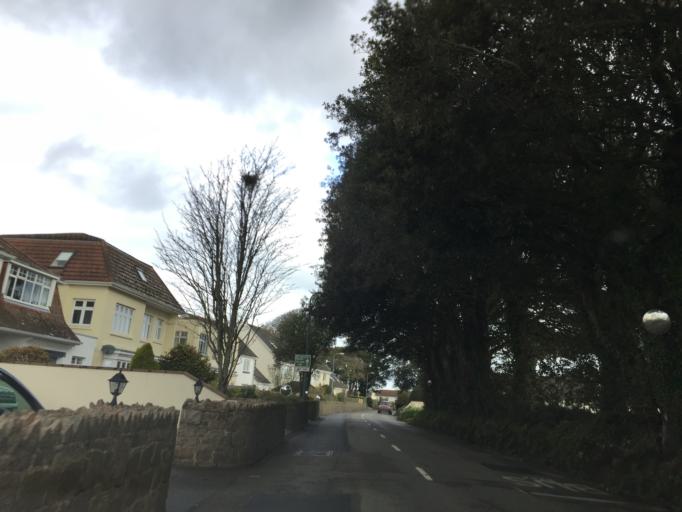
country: JE
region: St Helier
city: Saint Helier
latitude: 49.2060
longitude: -2.1428
